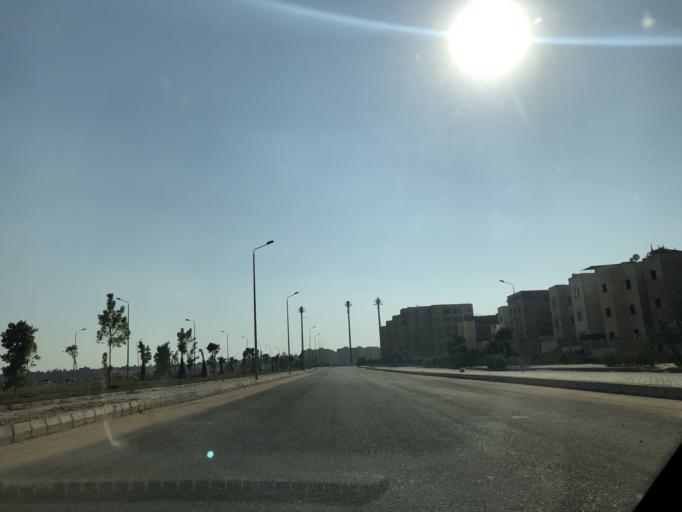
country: EG
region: Al Jizah
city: Madinat Sittah Uktubar
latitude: 29.9210
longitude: 31.0655
